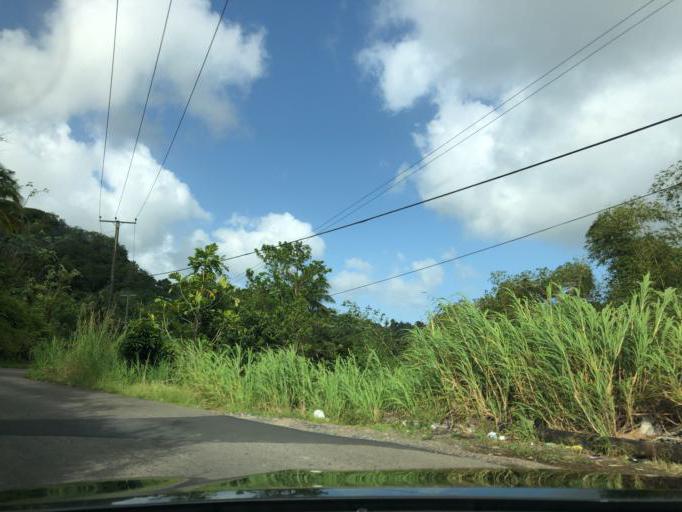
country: LC
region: Castries Quarter
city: Bisee
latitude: 13.9923
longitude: -60.9573
